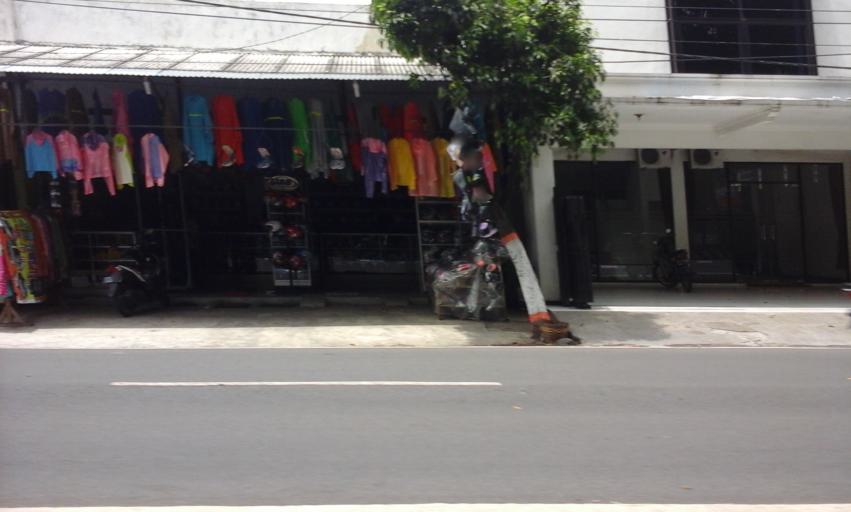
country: ID
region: East Java
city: Sukodono
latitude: -8.1028
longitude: 113.2330
